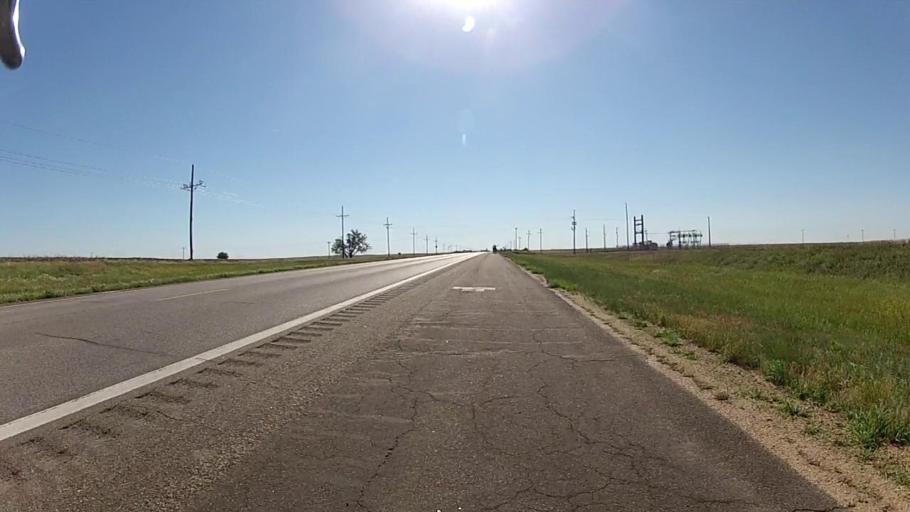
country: US
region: Kansas
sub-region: Kiowa County
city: Greensburg
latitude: 37.5863
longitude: -99.6146
